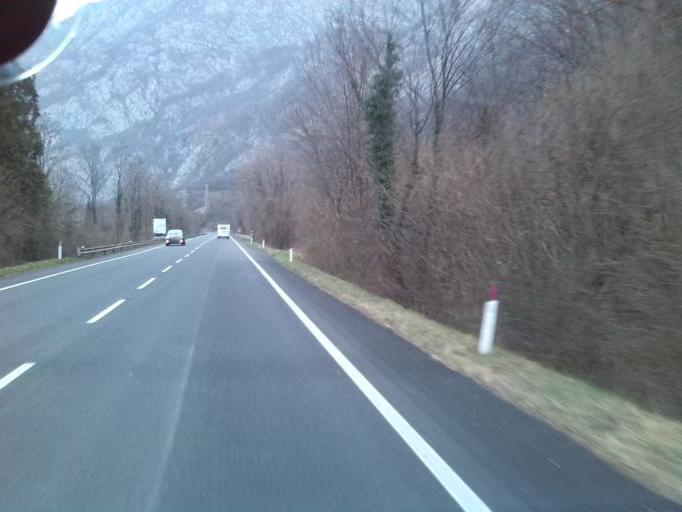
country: IT
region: Friuli Venezia Giulia
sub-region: Provincia di Udine
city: Venzone
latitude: 46.3459
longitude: 13.1408
